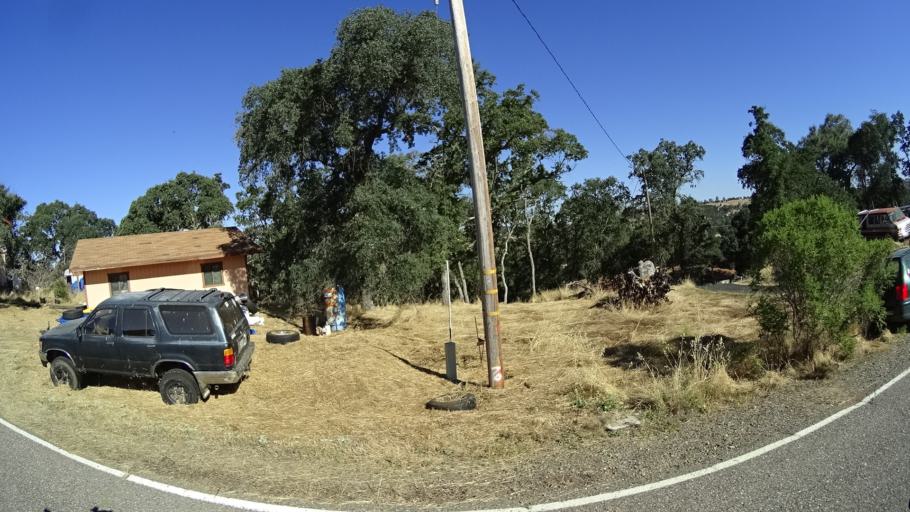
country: US
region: California
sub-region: Calaveras County
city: Rancho Calaveras
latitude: 38.1187
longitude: -120.8755
